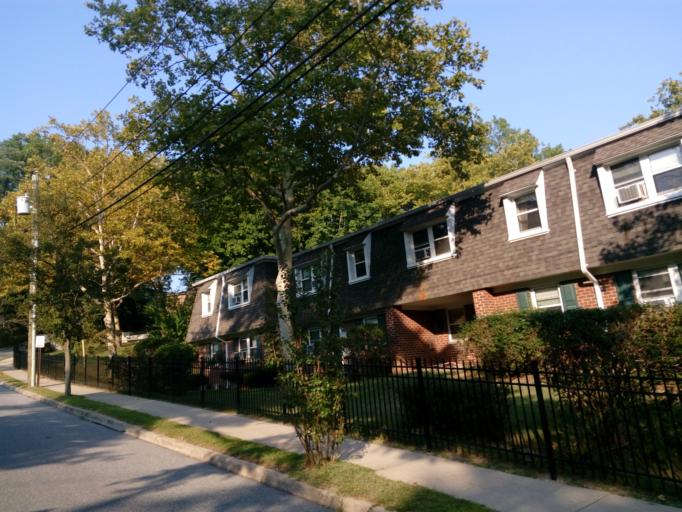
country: US
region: New York
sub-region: Nassau County
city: Glen Cove
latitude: 40.8639
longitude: -73.6242
